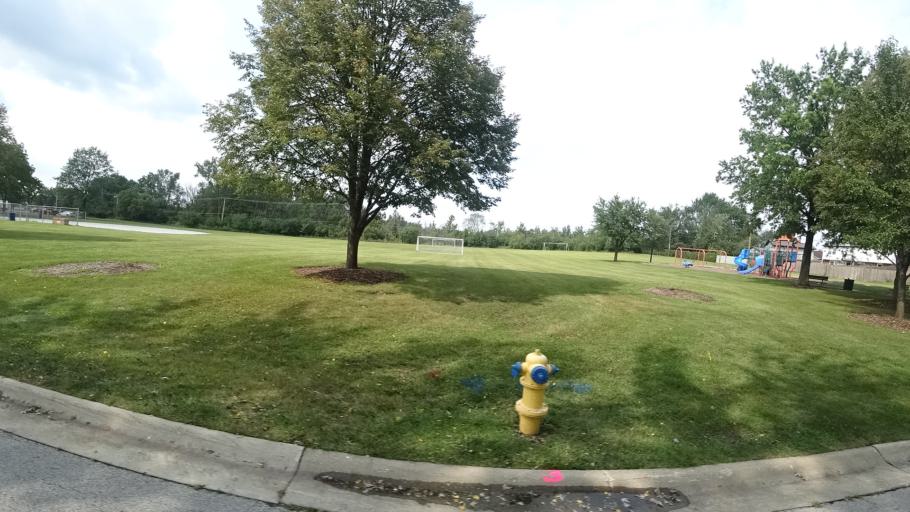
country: US
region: Illinois
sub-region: Cook County
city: Tinley Park
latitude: 41.5942
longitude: -87.7833
